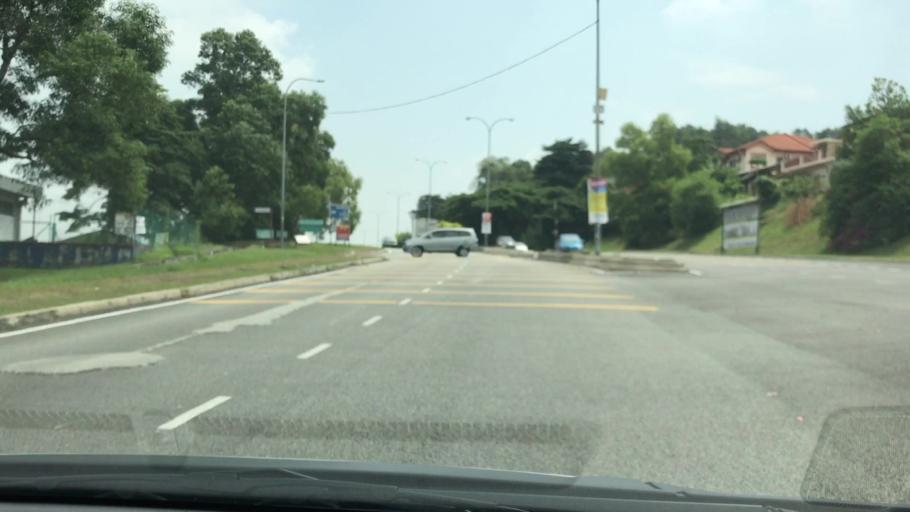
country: MY
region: Putrajaya
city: Putrajaya
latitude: 2.9881
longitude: 101.6643
